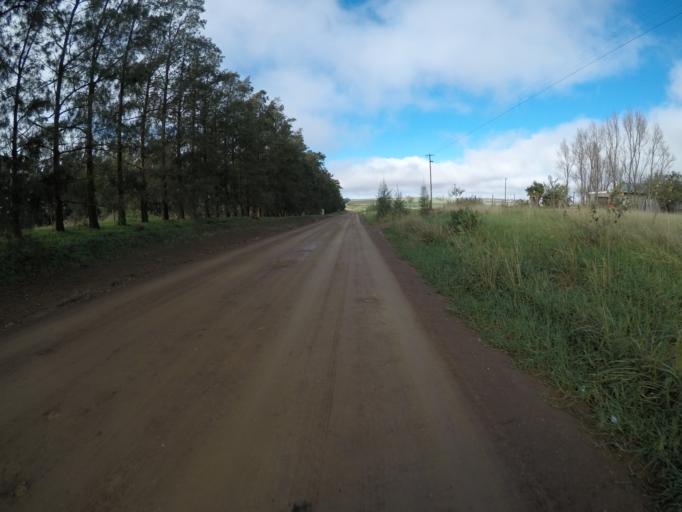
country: ZA
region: Western Cape
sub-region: Cape Winelands District Municipality
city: Ashton
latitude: -34.1419
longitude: 19.8638
